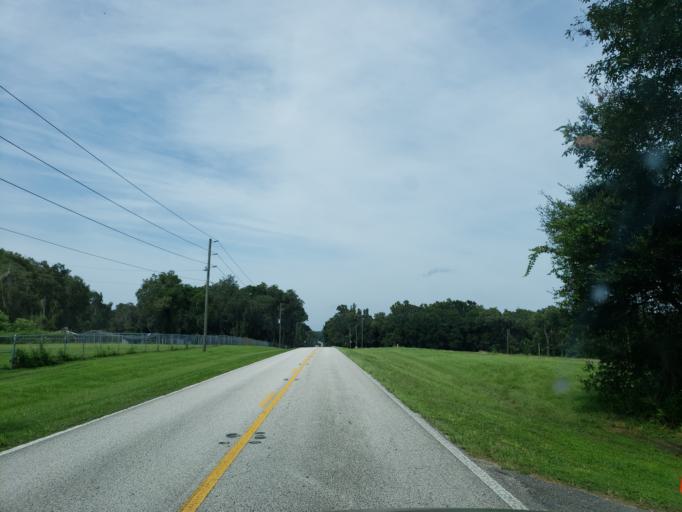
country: US
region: Florida
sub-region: Pasco County
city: San Antonio
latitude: 28.4108
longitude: -82.3093
